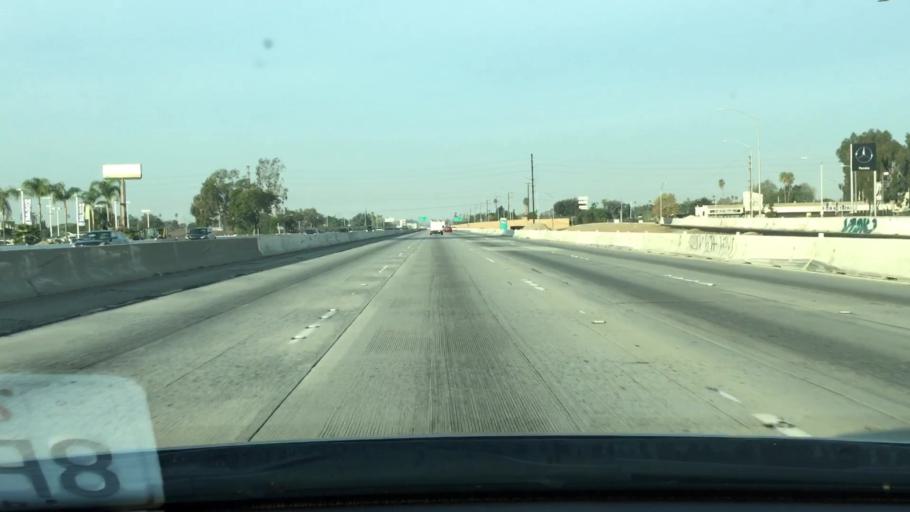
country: US
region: California
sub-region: Los Angeles County
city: Covina
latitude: 34.0722
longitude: -117.9051
